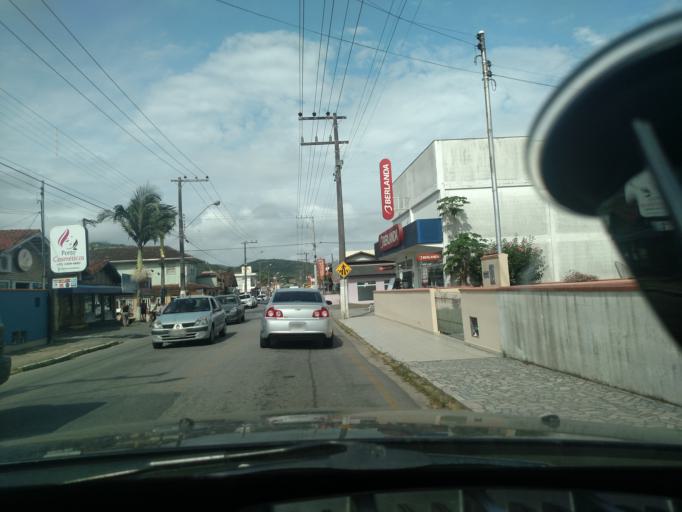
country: BR
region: Santa Catarina
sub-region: Porto Belo
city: Porto Belo
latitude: -27.1534
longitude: -48.5401
